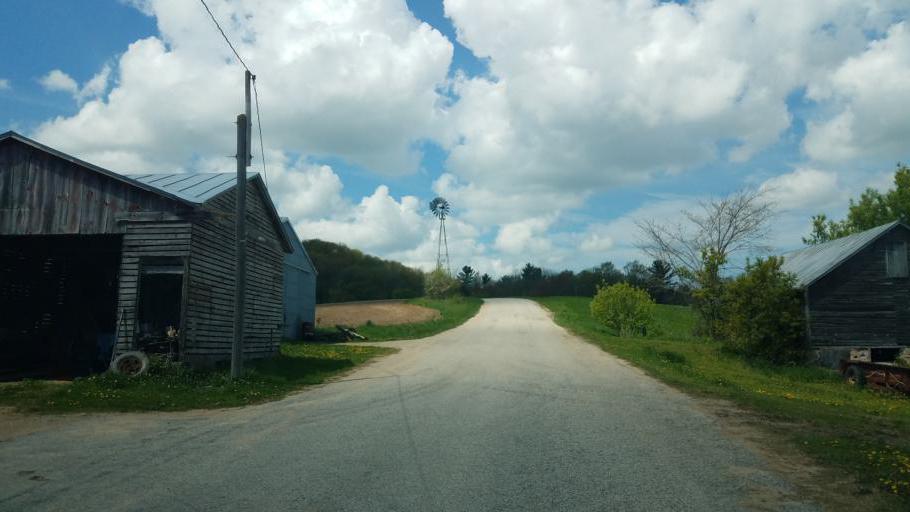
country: US
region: Wisconsin
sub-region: Vernon County
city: Hillsboro
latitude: 43.6941
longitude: -90.3123
